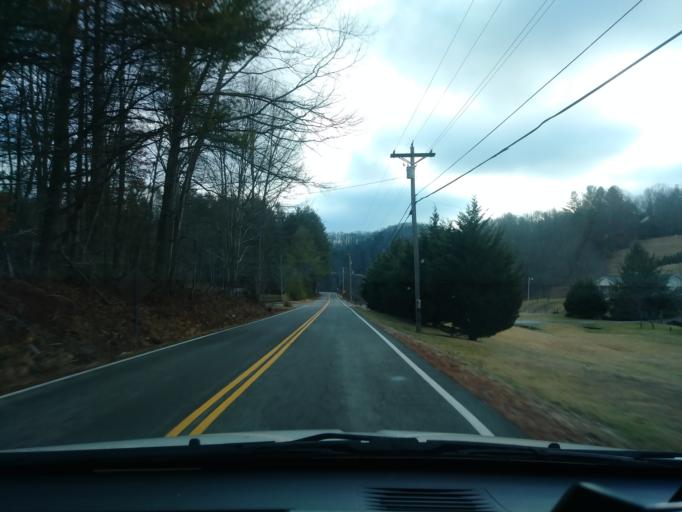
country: US
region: Tennessee
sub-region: Unicoi County
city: Unicoi
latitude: 36.2105
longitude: -82.2258
